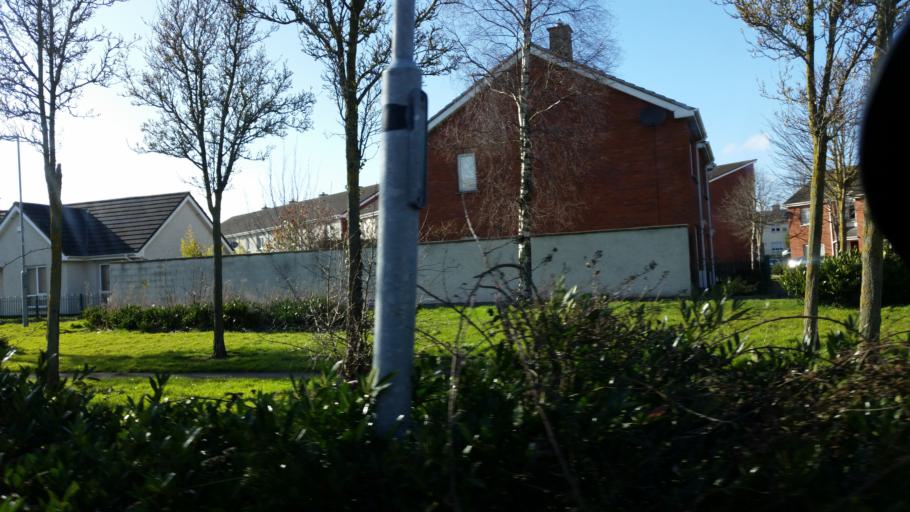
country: IE
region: Leinster
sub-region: Fingal County
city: Blanchardstown
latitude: 53.4035
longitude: -6.3873
